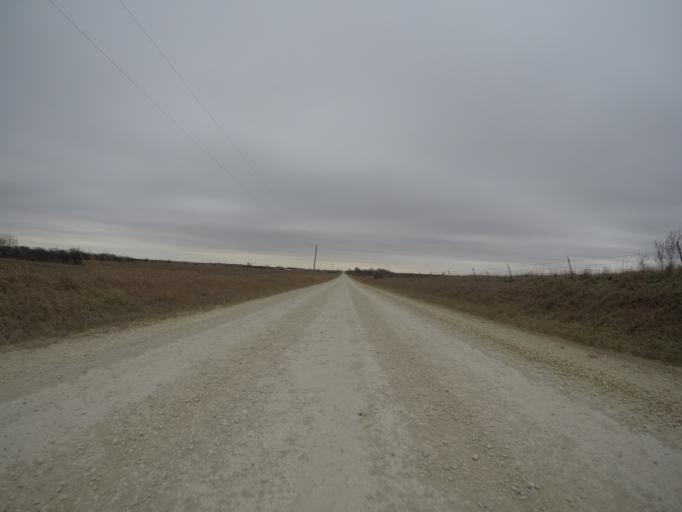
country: US
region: Kansas
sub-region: Wabaunsee County
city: Alma
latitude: 38.8455
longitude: -96.1133
